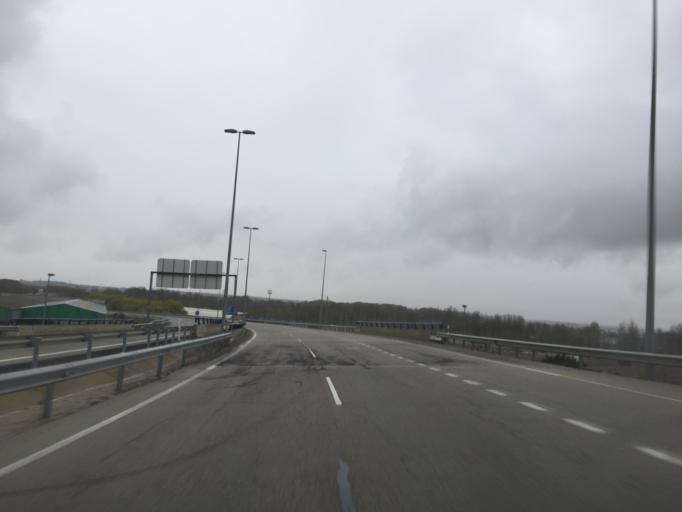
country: ES
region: Castille and Leon
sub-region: Provincia de Leon
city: Leon
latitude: 42.5756
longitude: -5.5559
